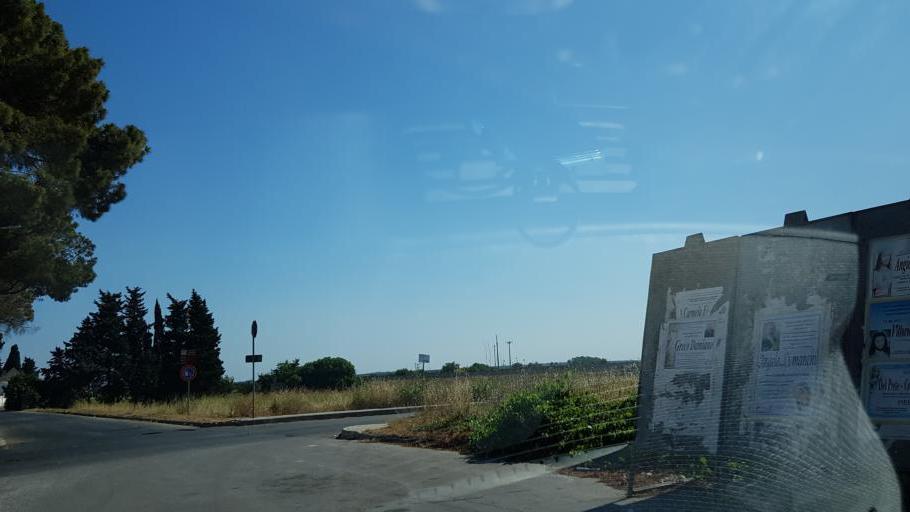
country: IT
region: Apulia
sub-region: Provincia di Brindisi
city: San Donaci
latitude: 40.4450
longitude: 17.9212
